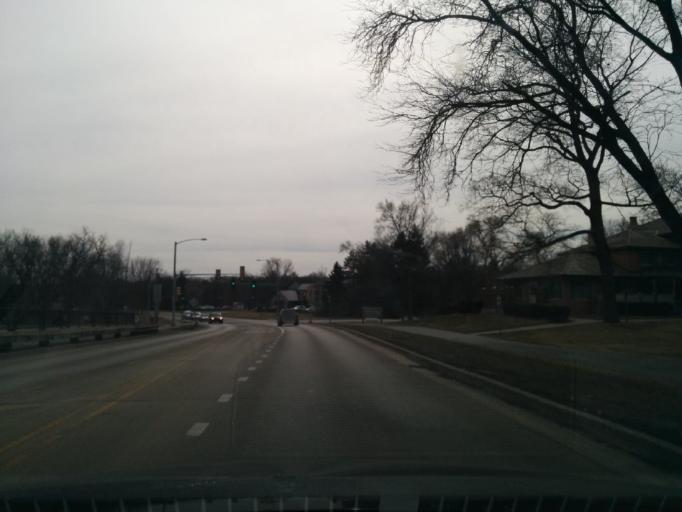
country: US
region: Illinois
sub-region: DuPage County
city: Oak Brook
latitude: 41.8203
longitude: -87.9272
